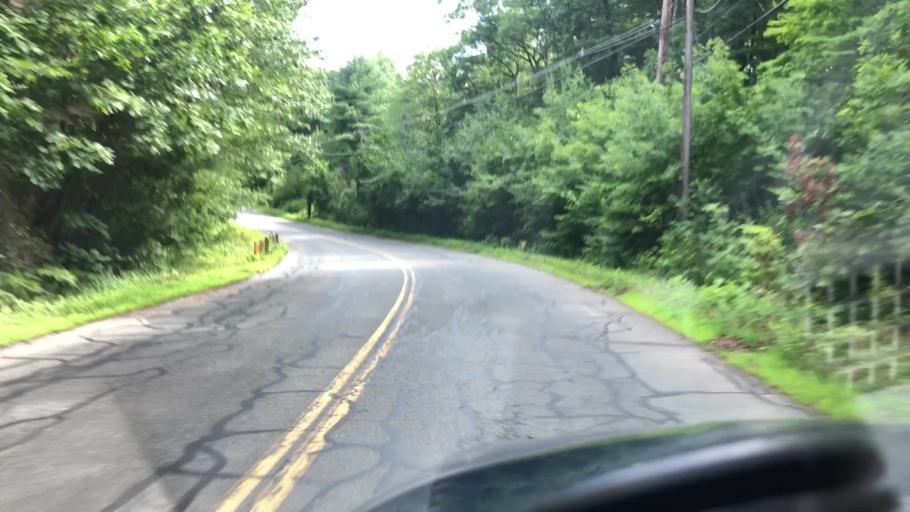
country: US
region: Massachusetts
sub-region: Hampden County
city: Holyoke
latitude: 42.1861
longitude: -72.6675
